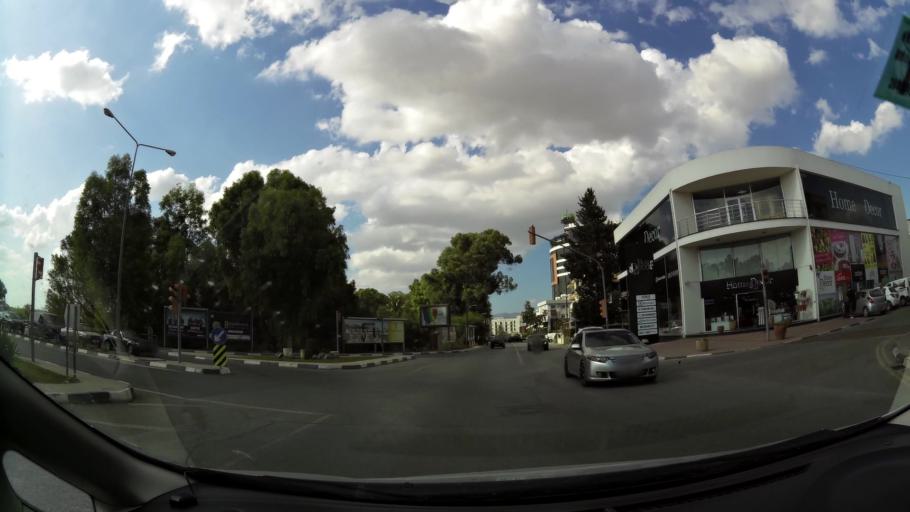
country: CY
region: Lefkosia
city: Nicosia
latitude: 35.1917
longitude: 33.3480
